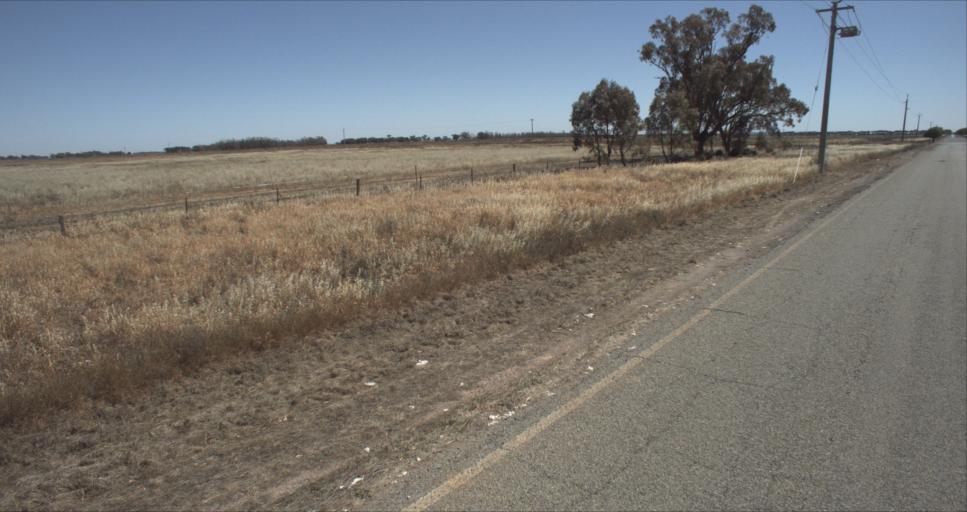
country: AU
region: New South Wales
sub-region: Leeton
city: Leeton
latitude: -34.4946
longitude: 146.2881
